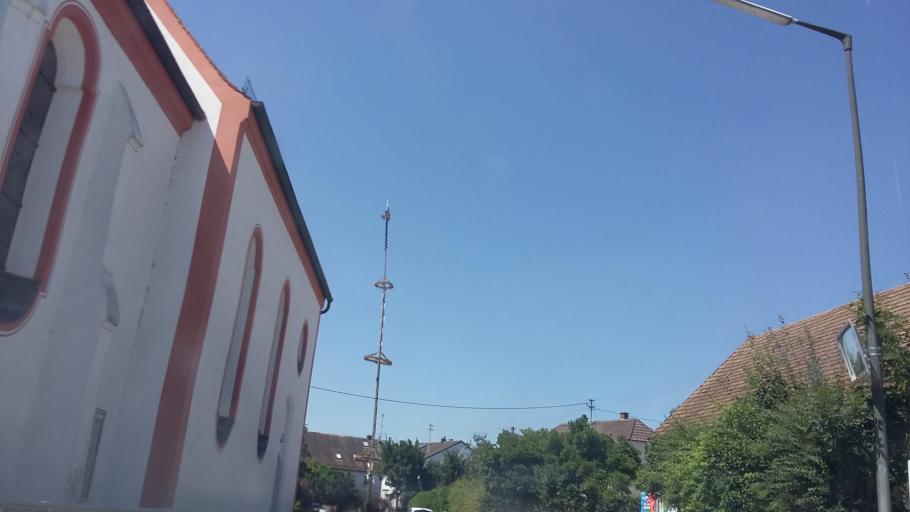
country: DE
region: Bavaria
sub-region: Upper Bavaria
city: Sulzemoos
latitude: 48.2698
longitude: 11.2695
